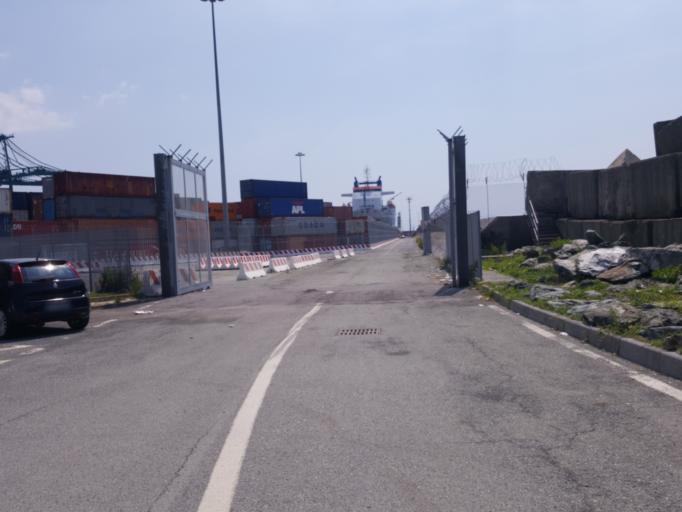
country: IT
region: Liguria
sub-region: Provincia di Genova
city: Mele
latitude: 44.4232
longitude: 8.7742
